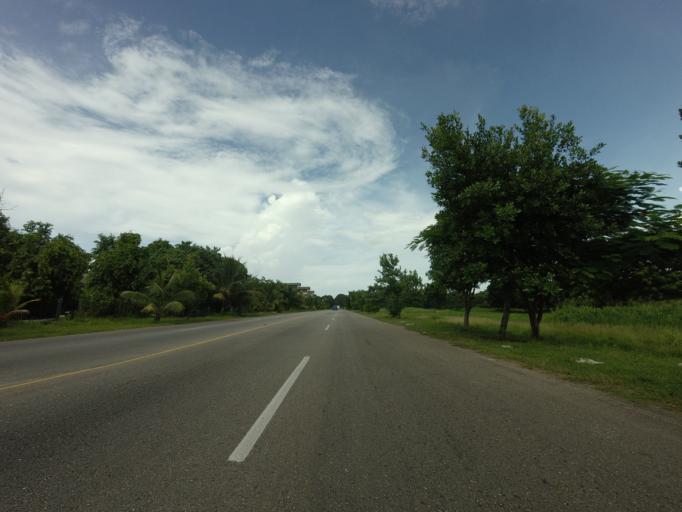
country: CU
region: La Habana
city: Cerro
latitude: 23.1065
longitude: -82.4371
